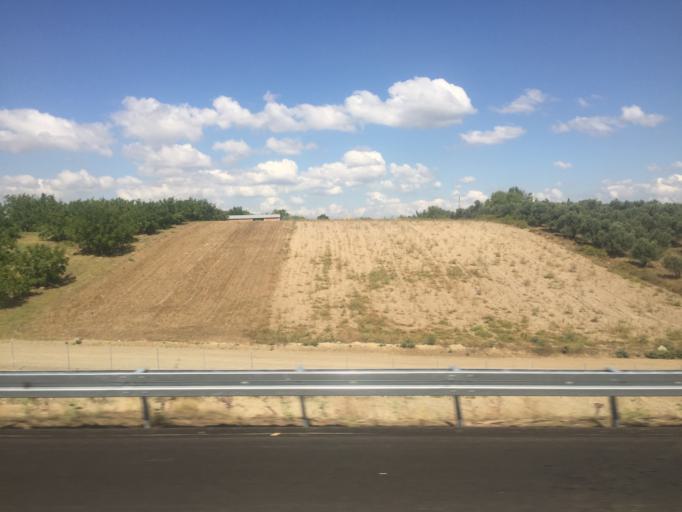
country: TR
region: Balikesir
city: Gobel
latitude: 40.0510
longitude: 28.2311
